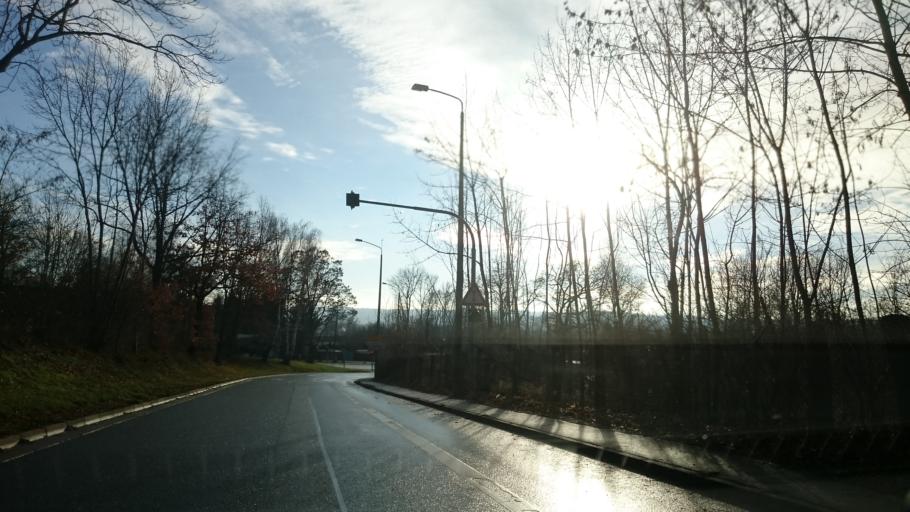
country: DE
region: Saxony
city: Zwickau
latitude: 50.7166
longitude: 12.5040
